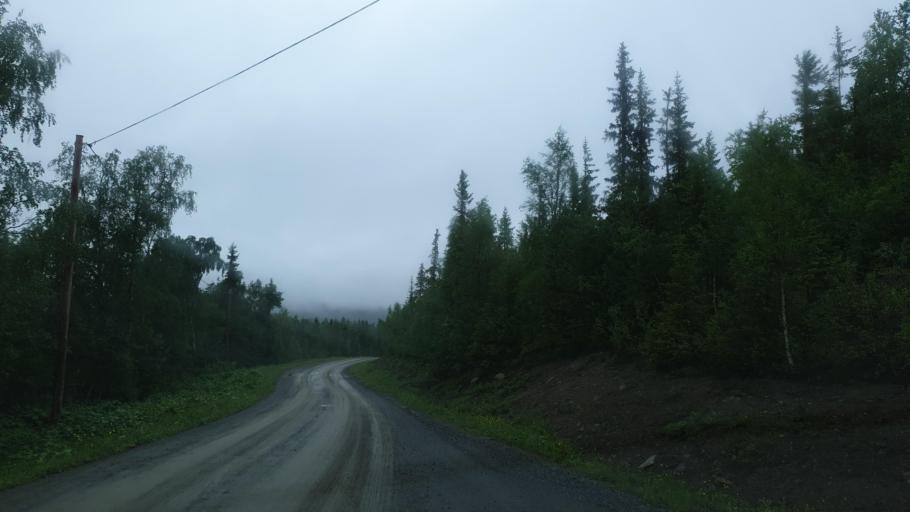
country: SE
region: Vaesterbotten
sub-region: Vilhelmina Kommun
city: Sjoberg
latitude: 65.3308
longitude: 15.8678
